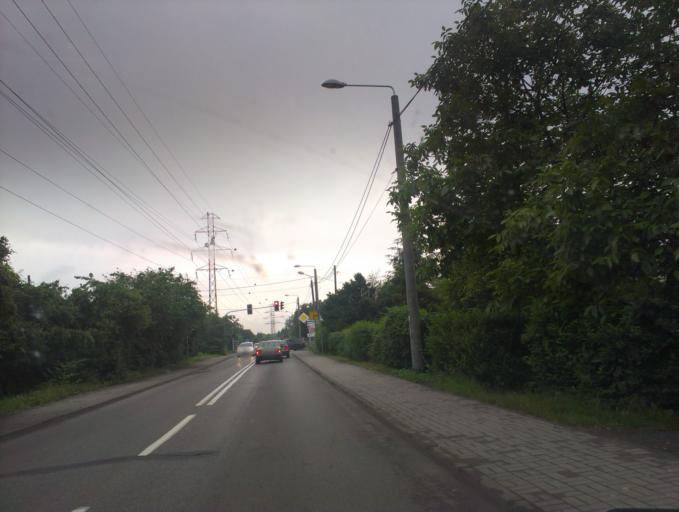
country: PL
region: Silesian Voivodeship
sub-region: Katowice
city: Katowice
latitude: 50.2430
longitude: 19.0192
